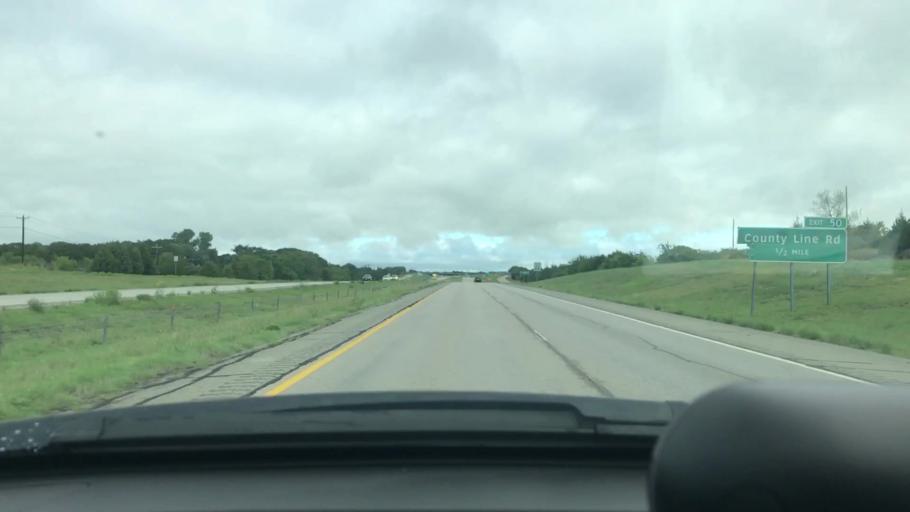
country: US
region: Texas
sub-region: Grayson County
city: Van Alstyne
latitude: 33.3896
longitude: -96.5805
